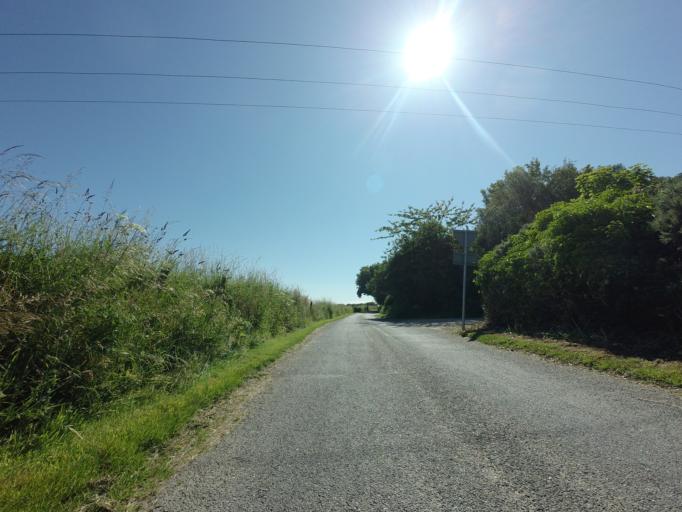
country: GB
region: Scotland
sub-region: Aberdeenshire
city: Macduff
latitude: 57.6604
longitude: -2.4950
